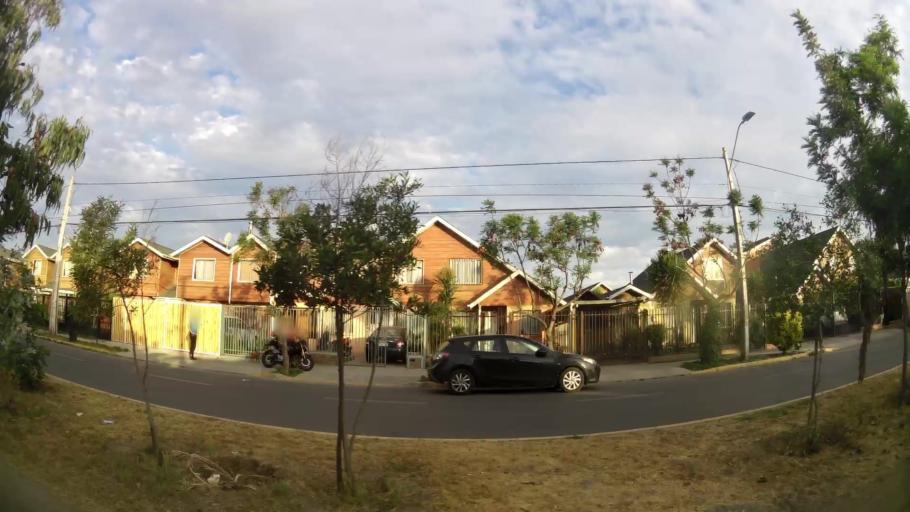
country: CL
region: Santiago Metropolitan
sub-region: Provincia de Maipo
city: San Bernardo
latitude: -33.6239
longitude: -70.6867
